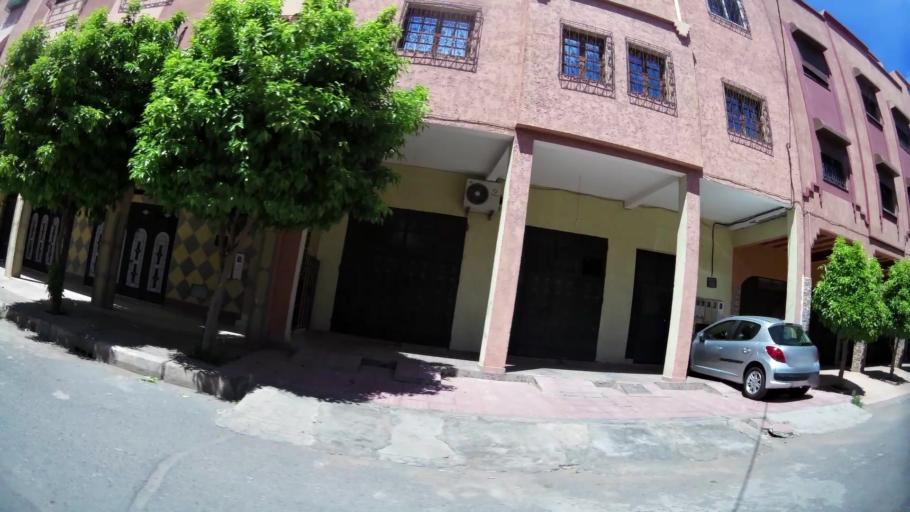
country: MA
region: Marrakech-Tensift-Al Haouz
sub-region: Marrakech
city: Marrakesh
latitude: 31.6403
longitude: -8.0644
